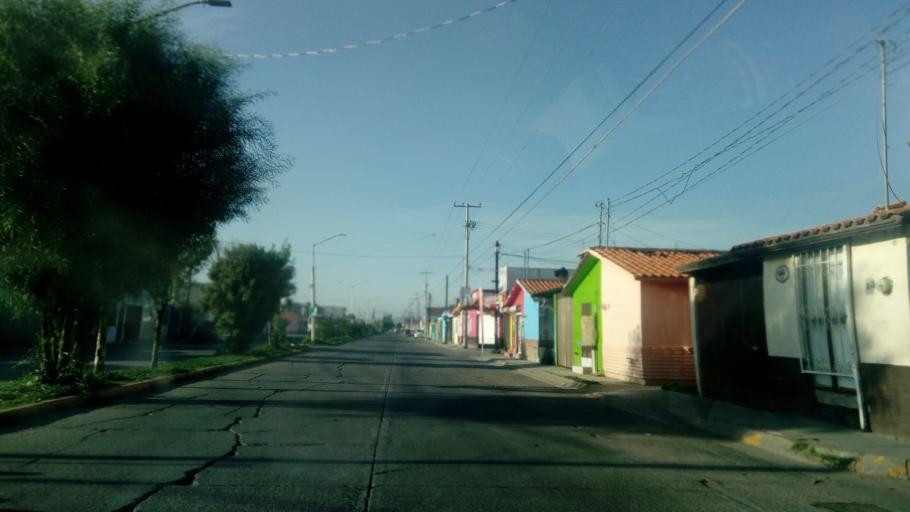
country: MX
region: Durango
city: Victoria de Durango
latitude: 24.0642
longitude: -104.5857
